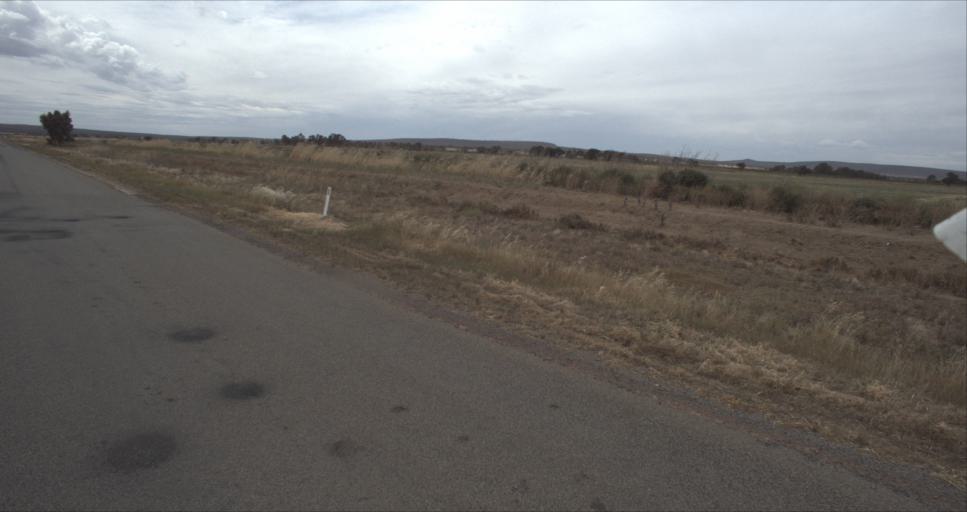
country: AU
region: New South Wales
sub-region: Leeton
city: Leeton
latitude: -34.4963
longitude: 146.4005
